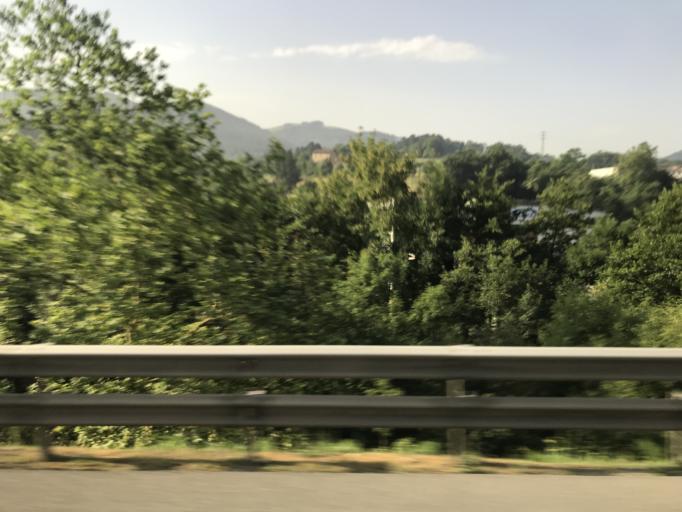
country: ES
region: Basque Country
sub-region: Provincia de Guipuzcoa
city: Idiazabal
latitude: 43.0255
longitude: -2.2247
